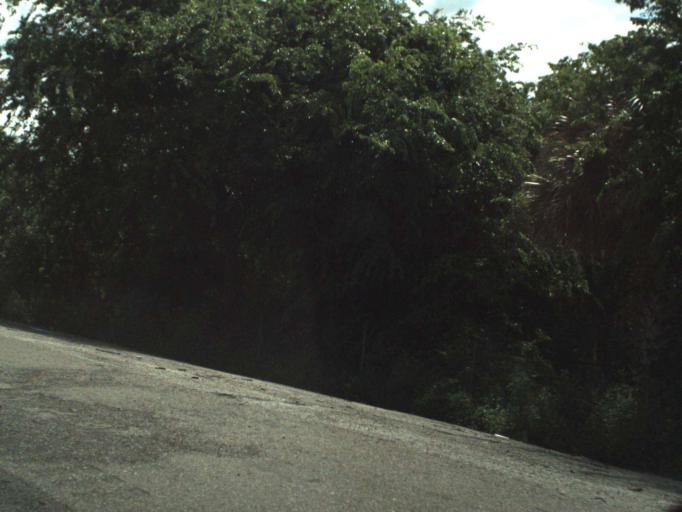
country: US
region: Florida
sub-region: Volusia County
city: DeBary
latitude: 28.8551
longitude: -81.2994
